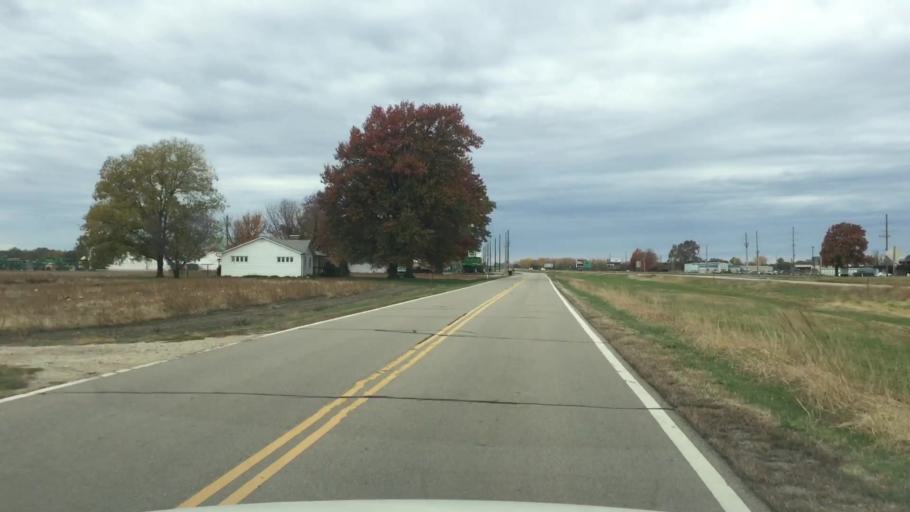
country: US
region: Kansas
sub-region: Shawnee County
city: Topeka
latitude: 39.0903
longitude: -95.6989
